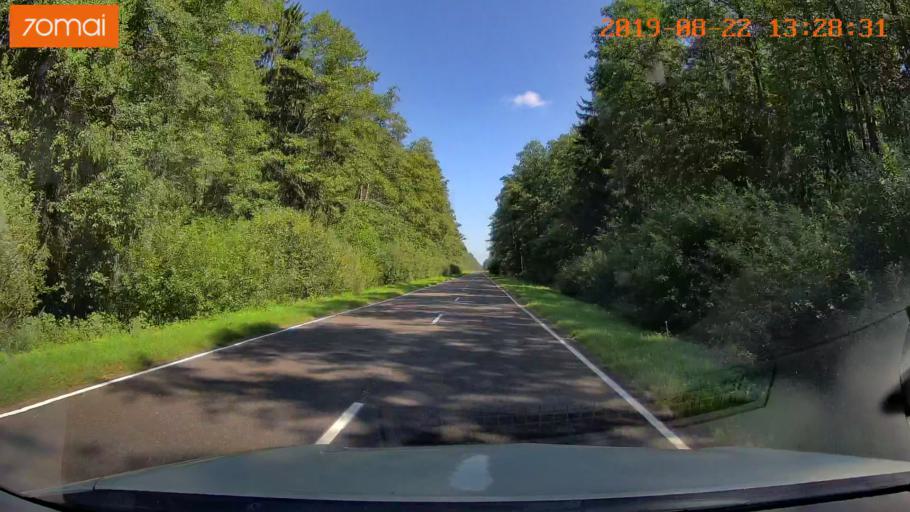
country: BY
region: Minsk
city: Staryya Darohi
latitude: 53.2126
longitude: 28.1100
